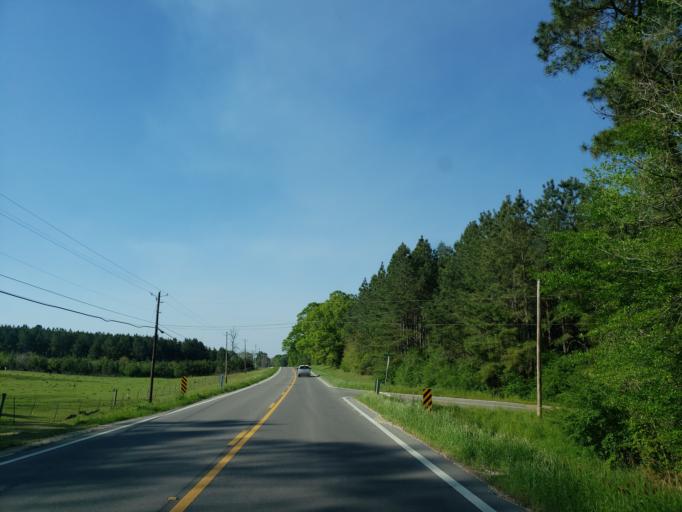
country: US
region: Mississippi
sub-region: Perry County
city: Richton
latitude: 31.3750
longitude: -88.9360
